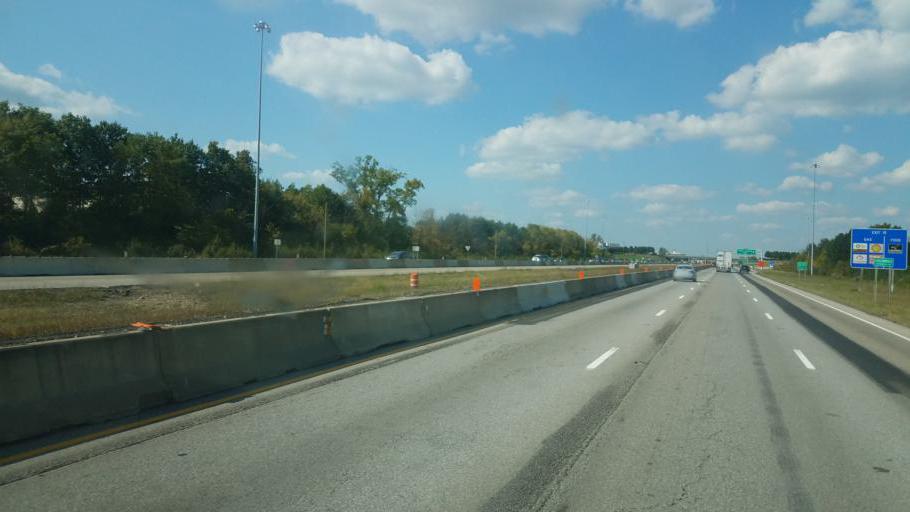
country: US
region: Ohio
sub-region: Franklin County
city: Dublin
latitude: 40.0691
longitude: -83.1336
